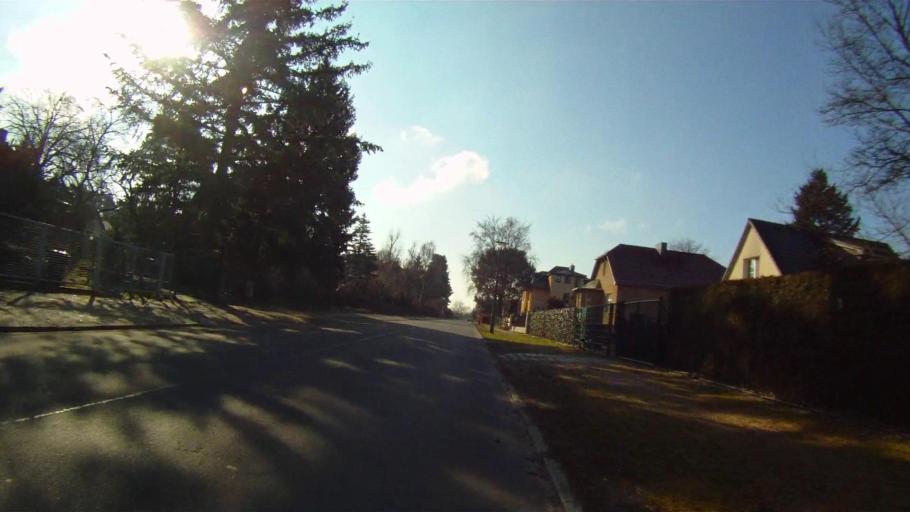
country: DE
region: Berlin
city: Rahnsdorf
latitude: 52.4397
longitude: 13.6993
